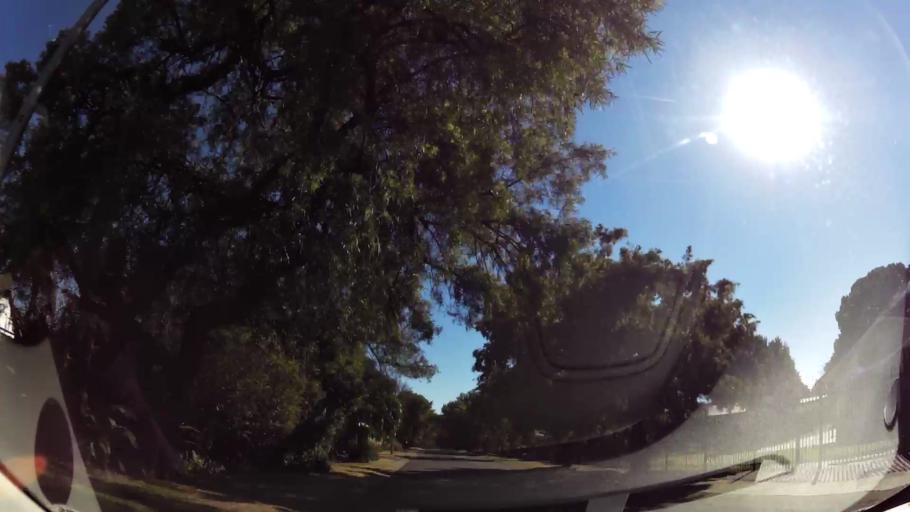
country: ZA
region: Gauteng
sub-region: City of Tshwane Metropolitan Municipality
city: Centurion
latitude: -25.8290
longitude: 28.2139
